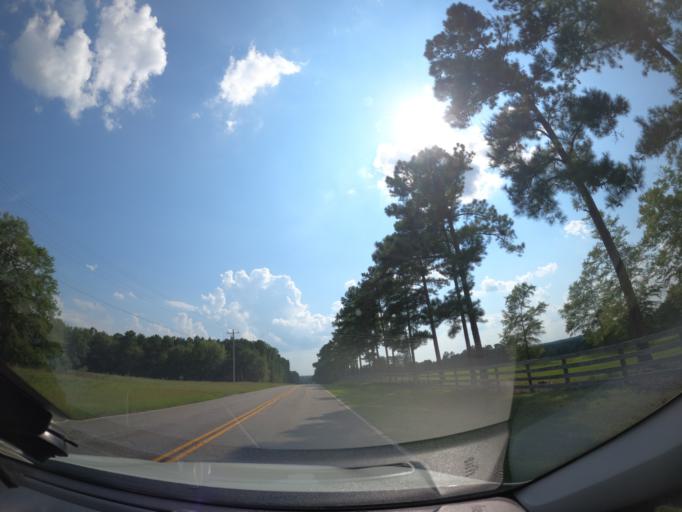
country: US
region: South Carolina
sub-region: Barnwell County
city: Williston
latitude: 33.5978
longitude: -81.4554
